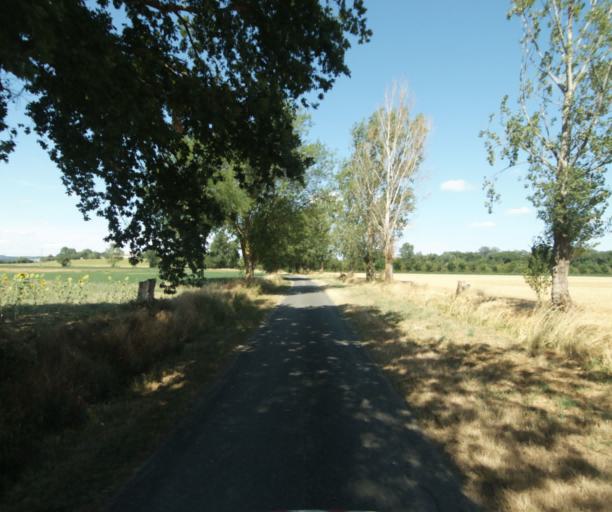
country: FR
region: Midi-Pyrenees
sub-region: Departement de la Haute-Garonne
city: Revel
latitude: 43.4933
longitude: 1.9926
